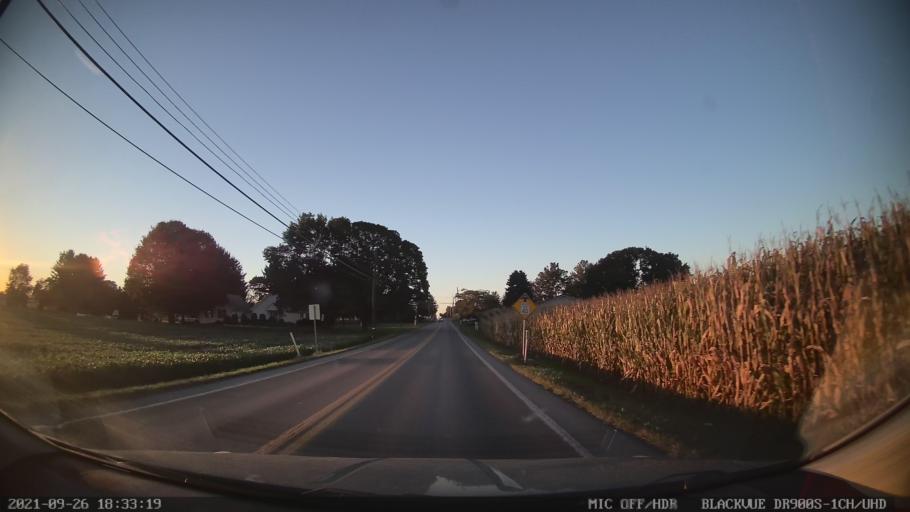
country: US
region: Pennsylvania
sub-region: Berks County
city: Kutztown
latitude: 40.4997
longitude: -75.7660
